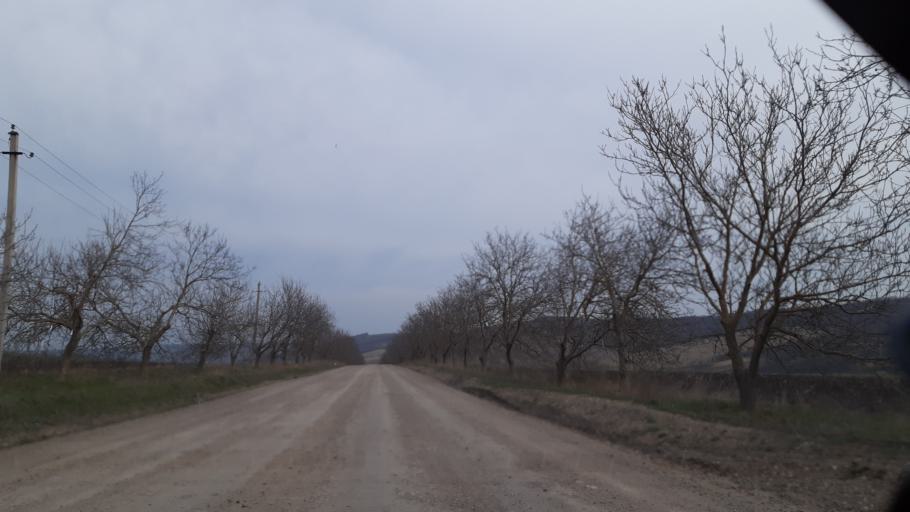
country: MD
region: Soldanesti
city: Soldanesti
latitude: 47.6920
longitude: 28.7383
